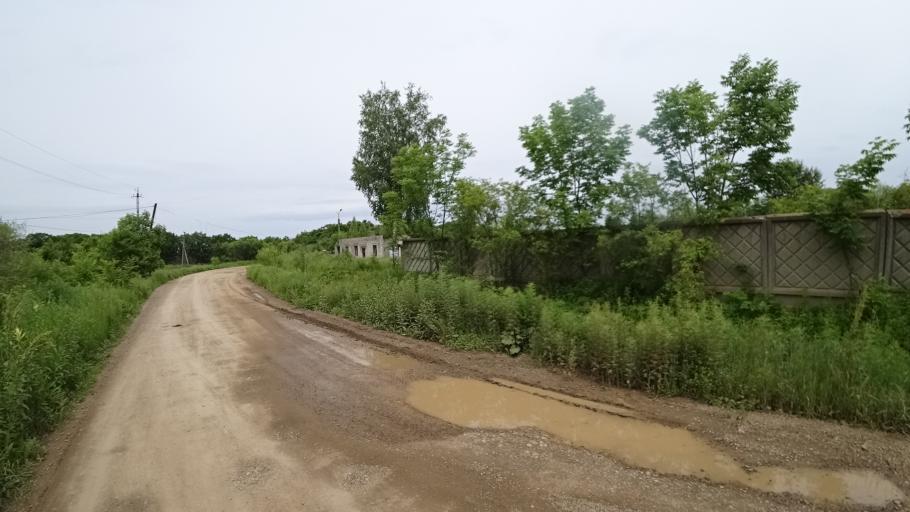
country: RU
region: Primorskiy
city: Arsen'yev
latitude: 44.1966
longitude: 133.3078
